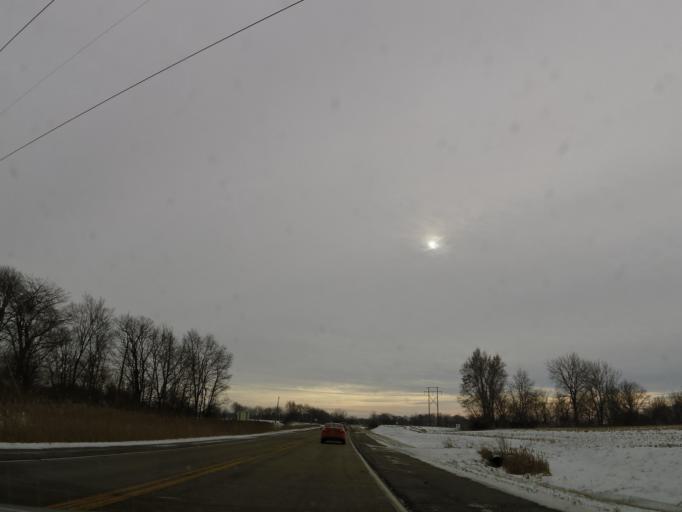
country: US
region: Illinois
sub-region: LaSalle County
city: Oglesby
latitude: 41.2724
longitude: -89.0784
